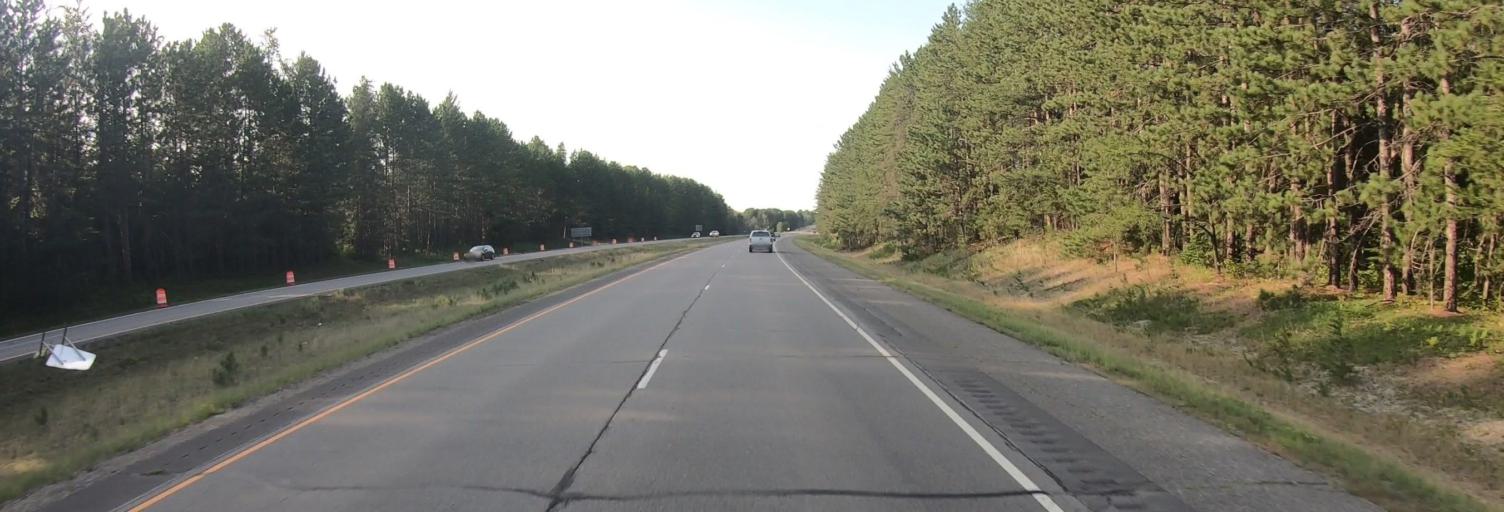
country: US
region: Minnesota
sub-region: Saint Louis County
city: Eveleth
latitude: 47.4053
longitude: -92.5195
